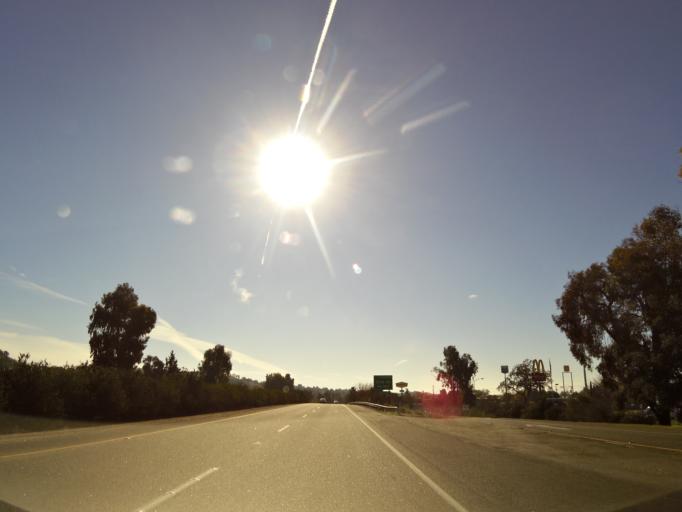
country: US
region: California
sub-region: San Luis Obispo County
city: Paso Robles
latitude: 35.6444
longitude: -120.6863
